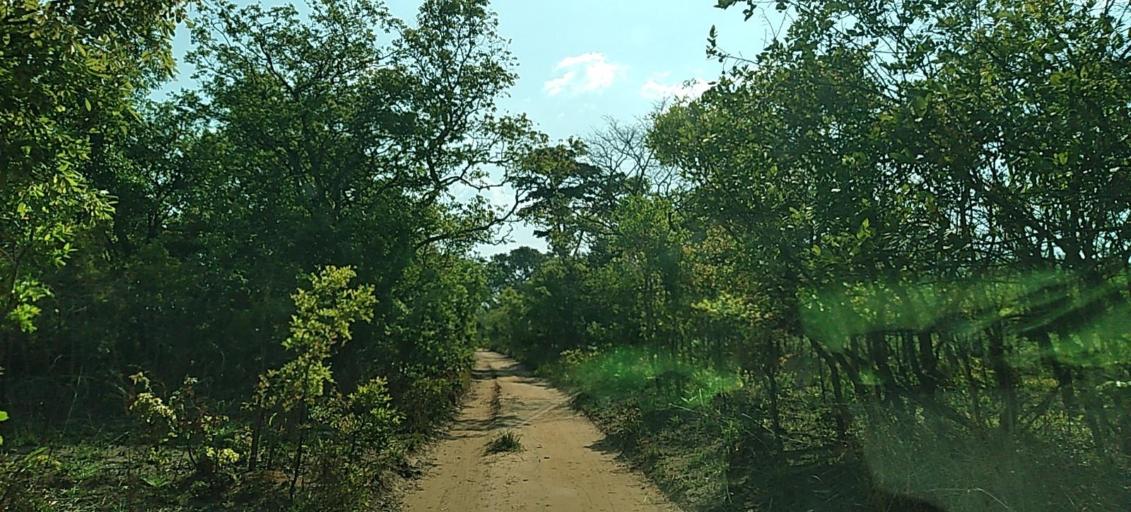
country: ZM
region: North-Western
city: Mwinilunga
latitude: -11.3003
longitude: 24.8496
